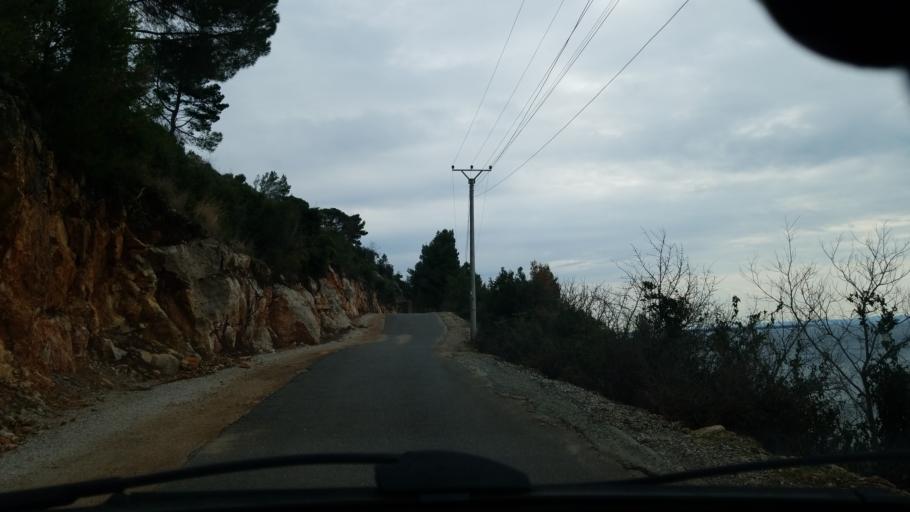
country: AL
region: Lezhe
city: Shengjin
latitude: 41.8168
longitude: 19.5680
